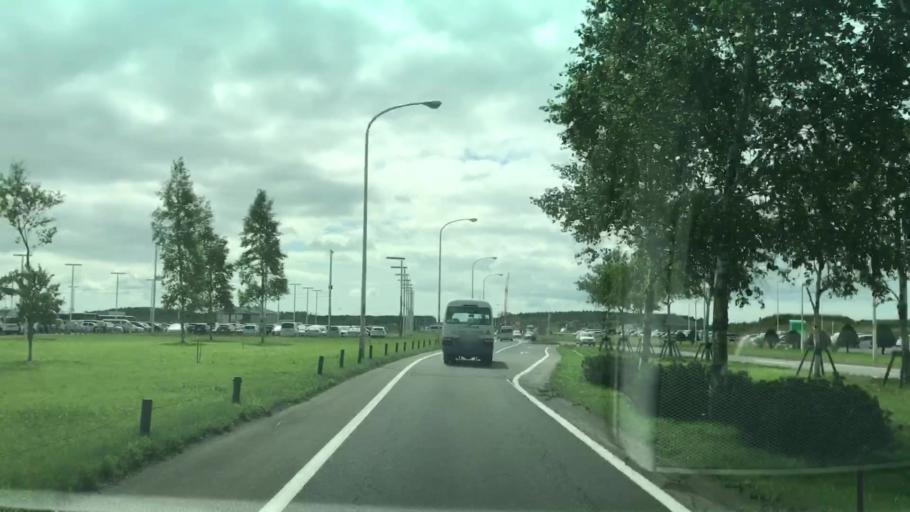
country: JP
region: Hokkaido
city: Chitose
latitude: 42.7822
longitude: 141.6777
